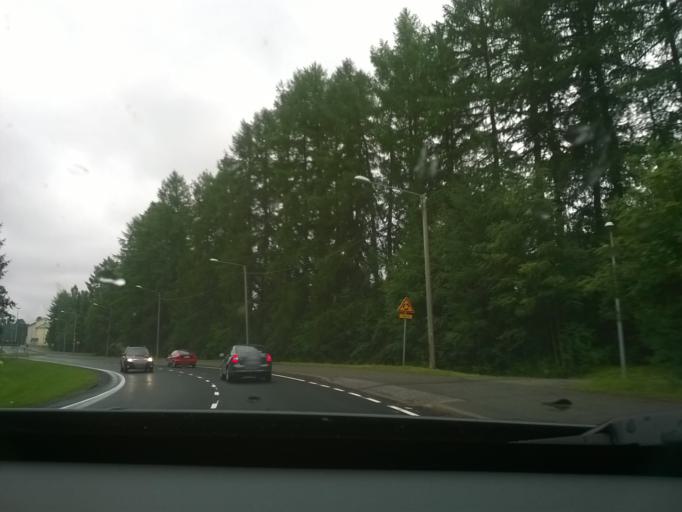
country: FI
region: Kainuu
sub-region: Kehys-Kainuu
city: Kuhmo
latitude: 64.1268
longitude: 29.5020
